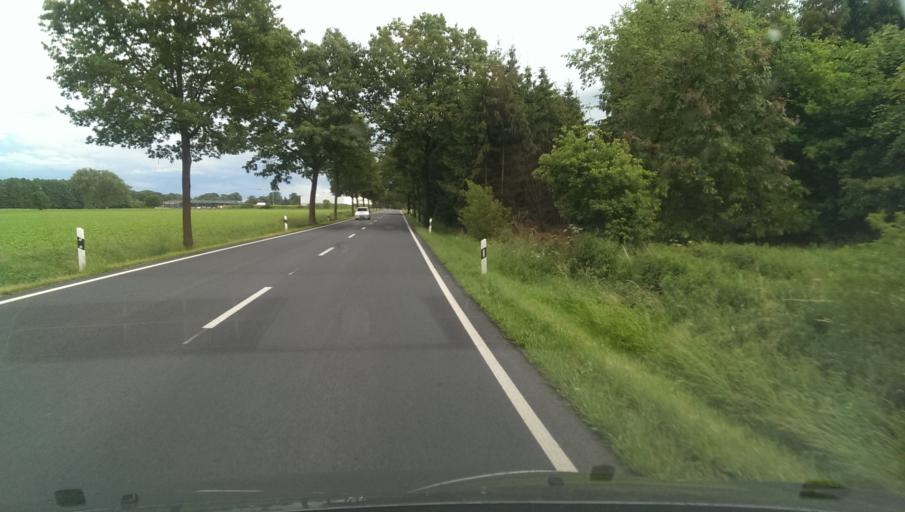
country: DE
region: Saxony-Anhalt
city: Jubar
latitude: 52.6553
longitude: 10.8585
